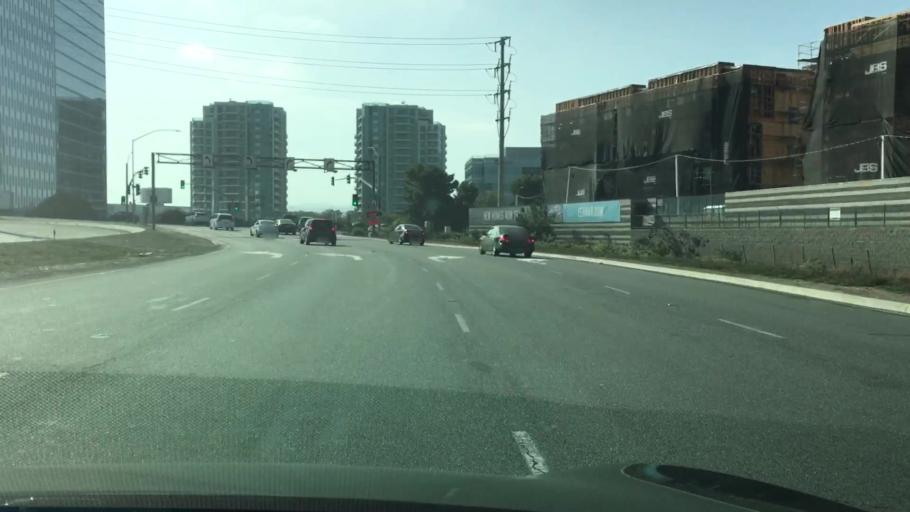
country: US
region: California
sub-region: Orange County
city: Irvine
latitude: 33.6765
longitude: -117.8456
